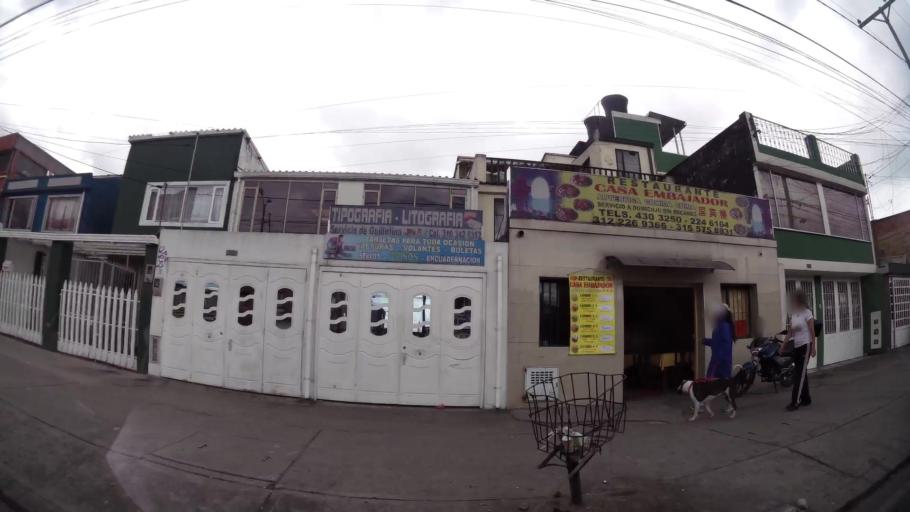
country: CO
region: Bogota D.C.
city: Barrio San Luis
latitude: 4.7097
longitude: -74.0941
